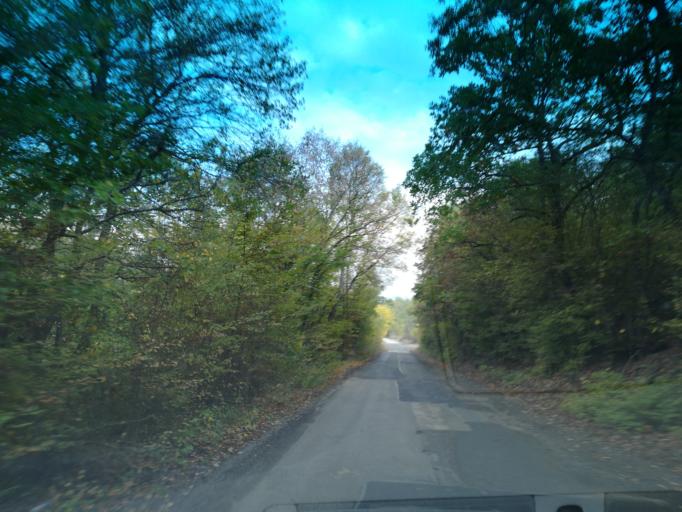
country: BG
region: Stara Zagora
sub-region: Obshtina Nikolaevo
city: Elkhovo
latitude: 42.3268
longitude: 25.3996
